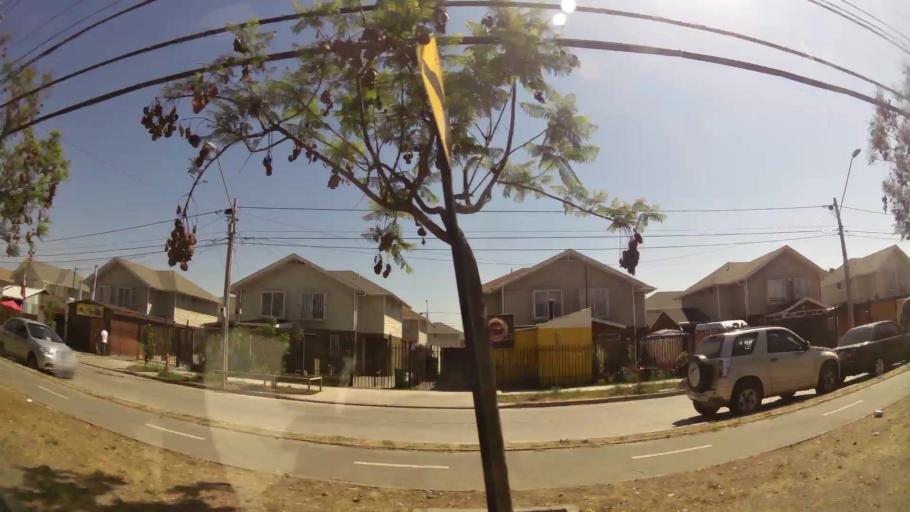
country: CL
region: Santiago Metropolitan
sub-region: Provincia de Maipo
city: San Bernardo
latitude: -33.6138
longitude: -70.6898
